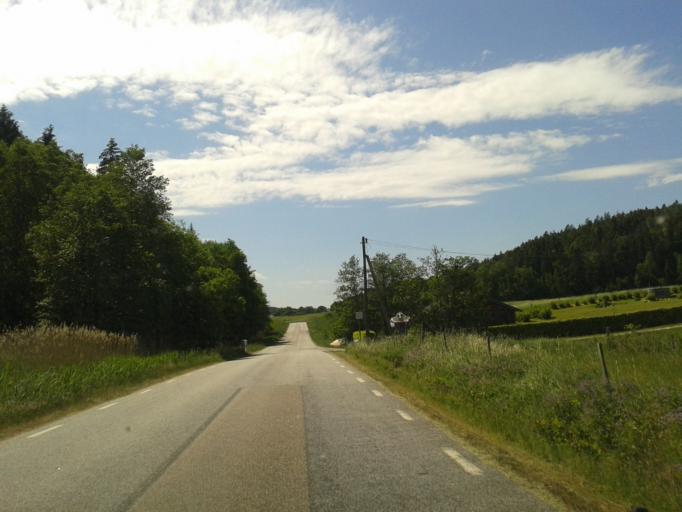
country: SE
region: Vaestra Goetaland
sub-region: Uddevalla Kommun
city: Uddevalla
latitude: 58.2993
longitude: 11.9504
